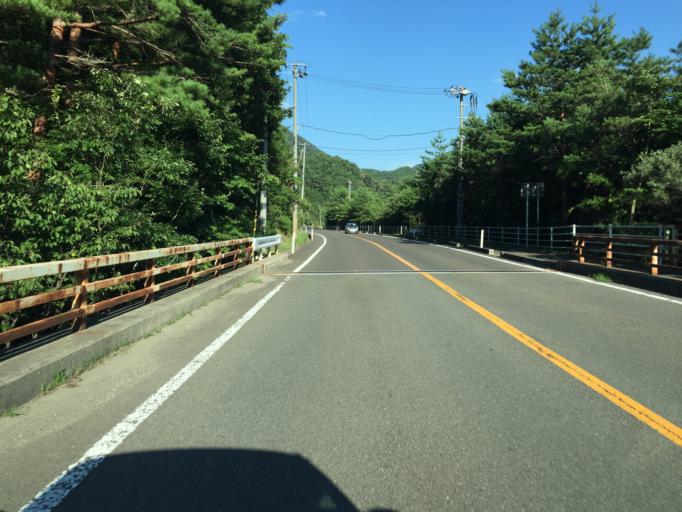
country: JP
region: Miyagi
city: Shiroishi
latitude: 37.9772
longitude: 140.4934
